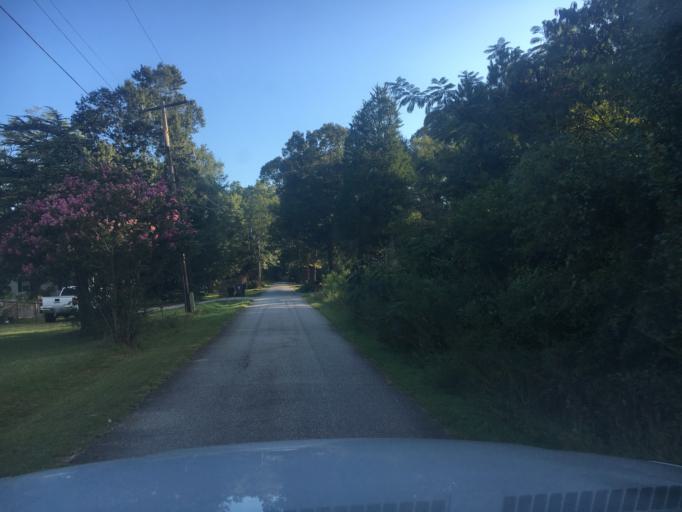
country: US
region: South Carolina
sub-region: Greenville County
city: Fountain Inn
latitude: 34.6062
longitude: -82.1099
